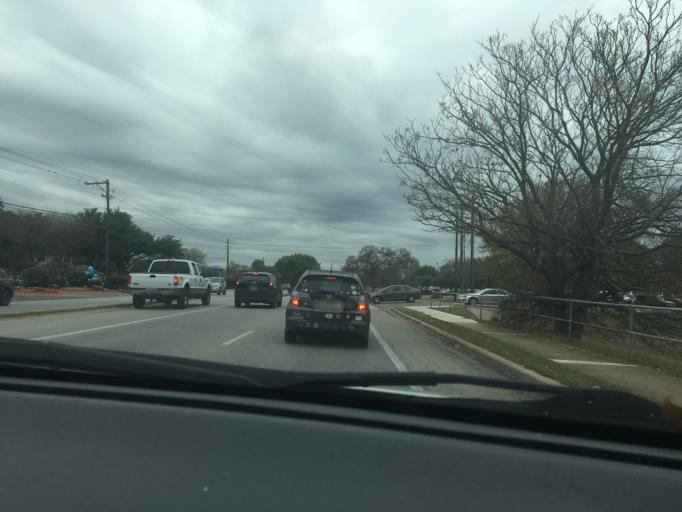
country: US
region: Texas
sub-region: Travis County
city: Shady Hollow
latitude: 30.2167
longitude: -97.8287
